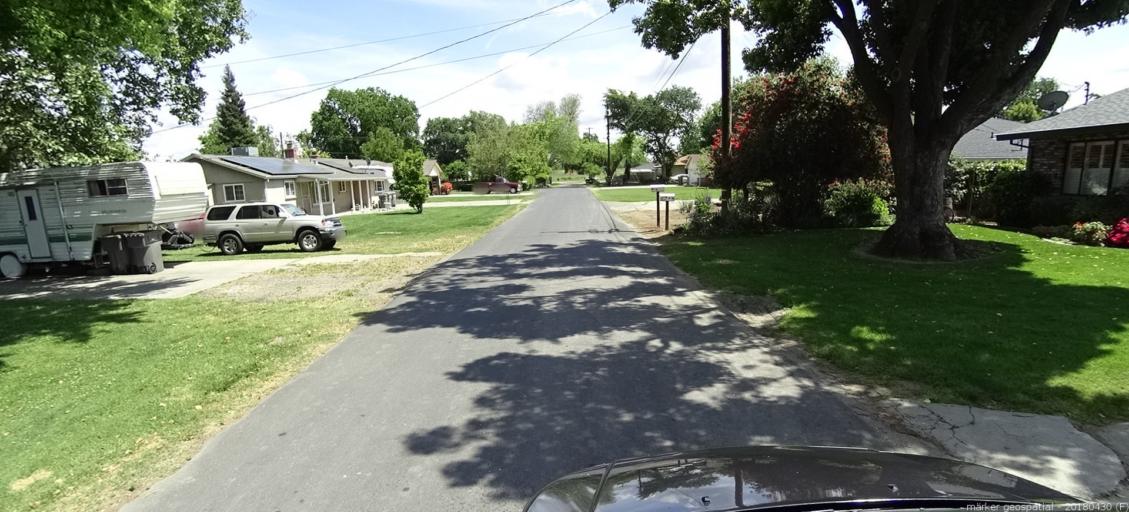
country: US
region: California
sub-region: Yolo County
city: West Sacramento
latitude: 38.5399
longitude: -121.5252
